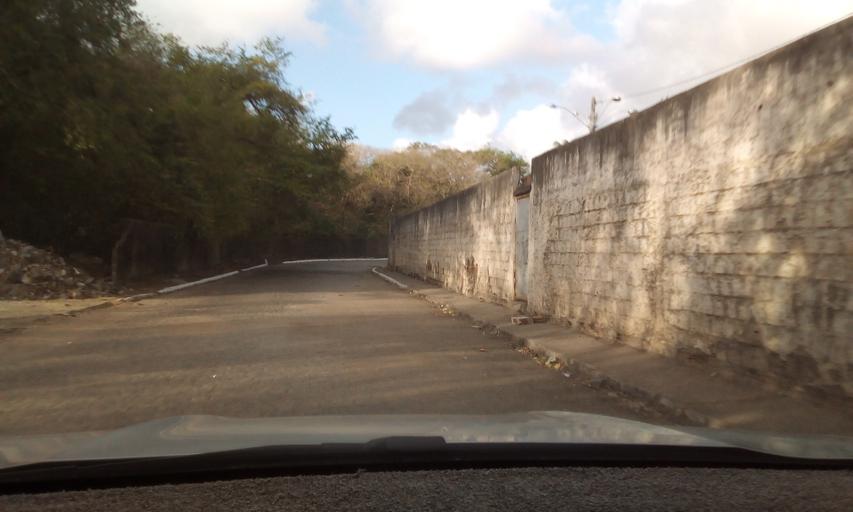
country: BR
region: Paraiba
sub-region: Bayeux
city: Bayeux
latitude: -7.1489
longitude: -34.8946
